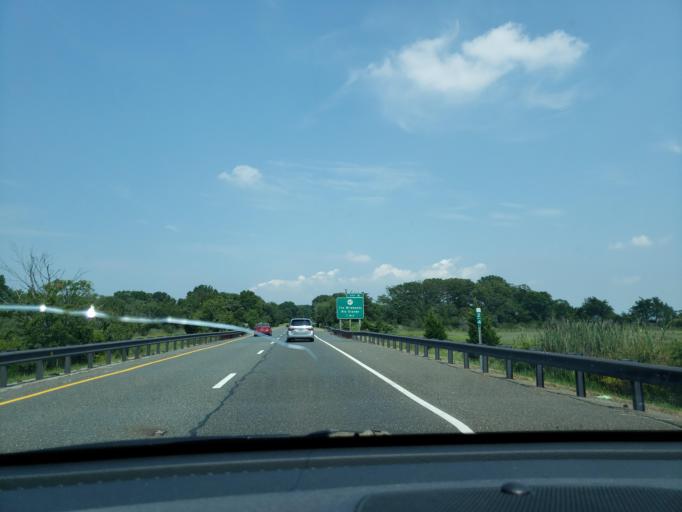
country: US
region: New Jersey
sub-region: Cape May County
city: Rio Grande
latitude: 38.9903
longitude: -74.8809
